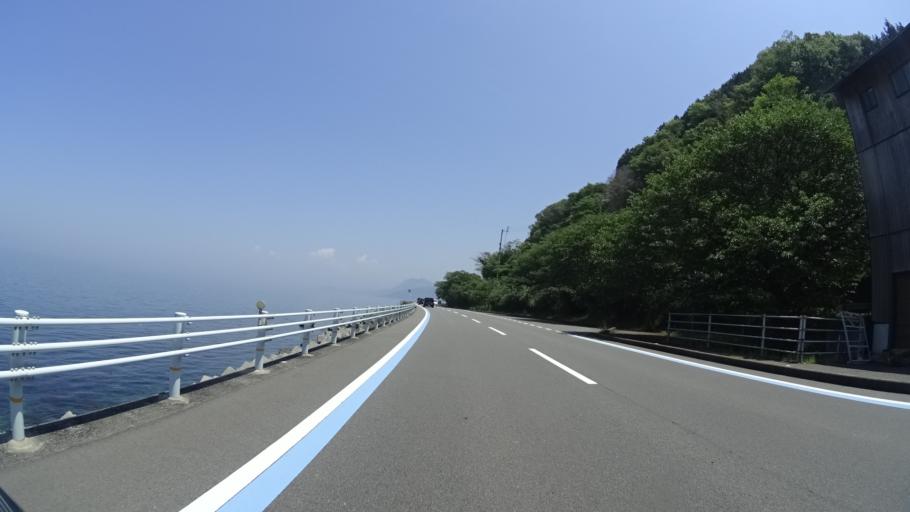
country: JP
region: Ehime
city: Ozu
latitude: 33.6447
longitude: 132.5541
